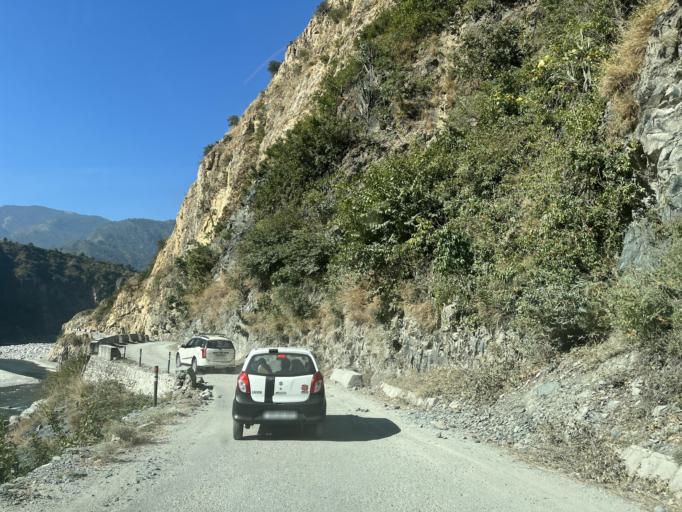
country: IN
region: Uttarakhand
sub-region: Naini Tal
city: Naini Tal
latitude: 29.5081
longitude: 79.4596
